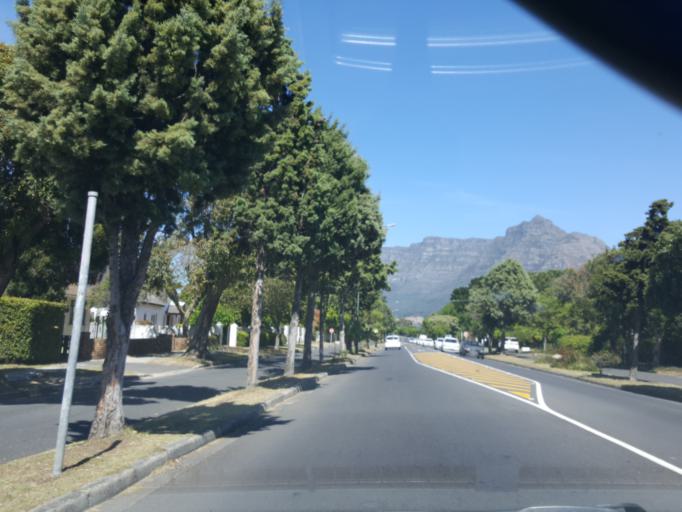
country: ZA
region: Western Cape
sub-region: City of Cape Town
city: Rosebank
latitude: -33.9429
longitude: 18.4964
